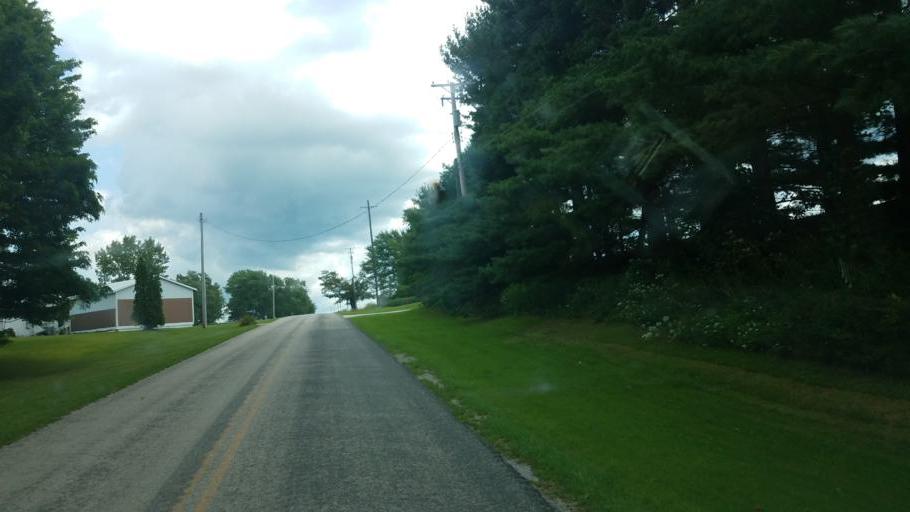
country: US
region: Ohio
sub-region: Ashtabula County
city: Roaming Shores
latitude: 41.5879
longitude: -80.7543
